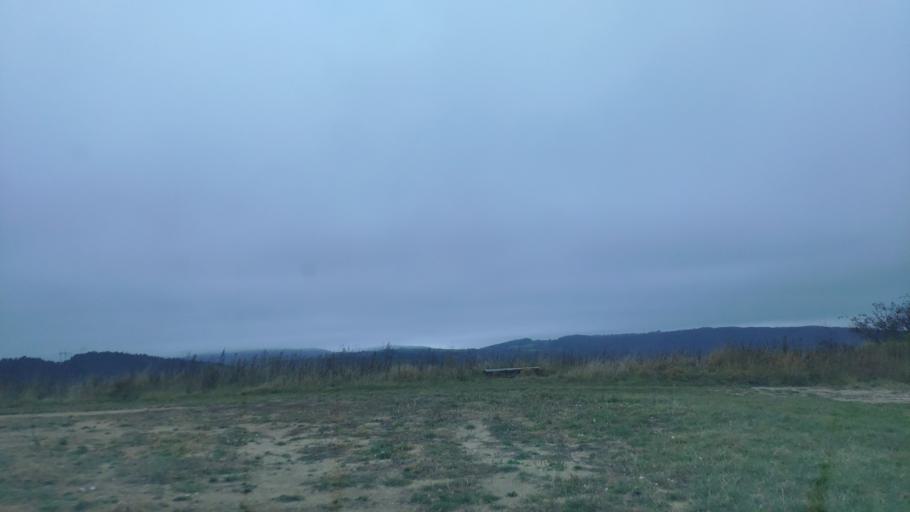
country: SK
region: Presovsky
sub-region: Okres Presov
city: Presov
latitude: 48.9331
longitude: 21.0887
